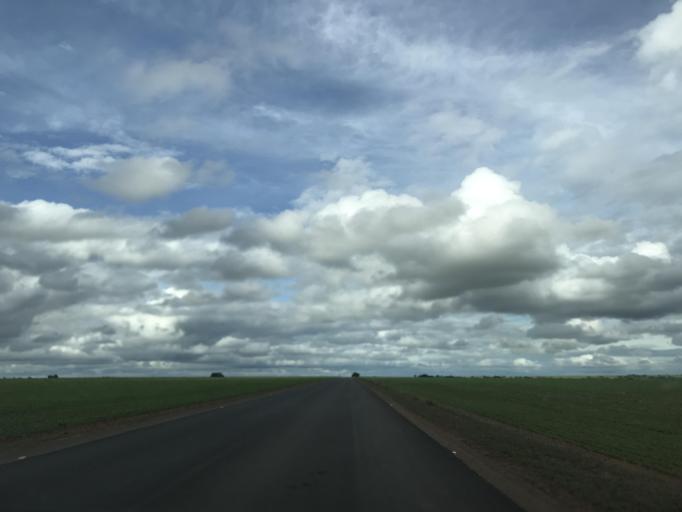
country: BR
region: Goias
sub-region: Vianopolis
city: Vianopolis
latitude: -16.9704
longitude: -48.6546
